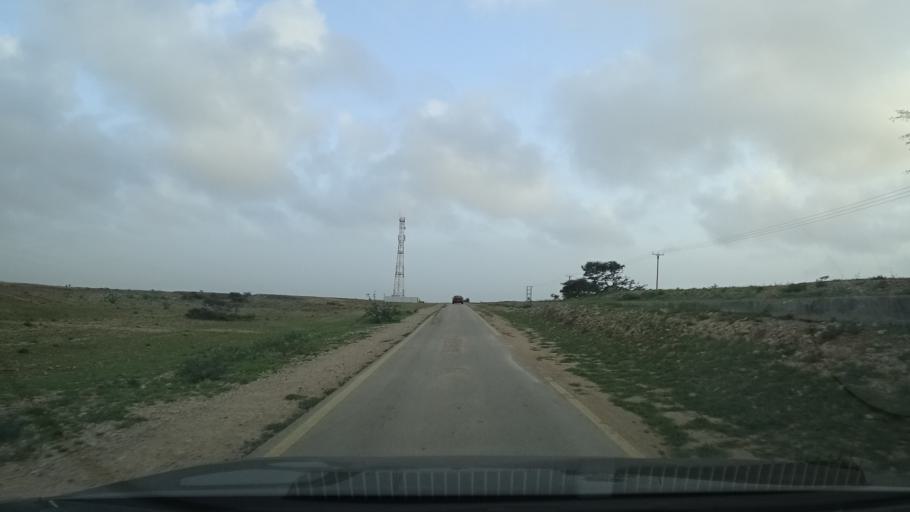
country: OM
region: Zufar
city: Salalah
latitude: 17.0889
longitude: 54.2326
